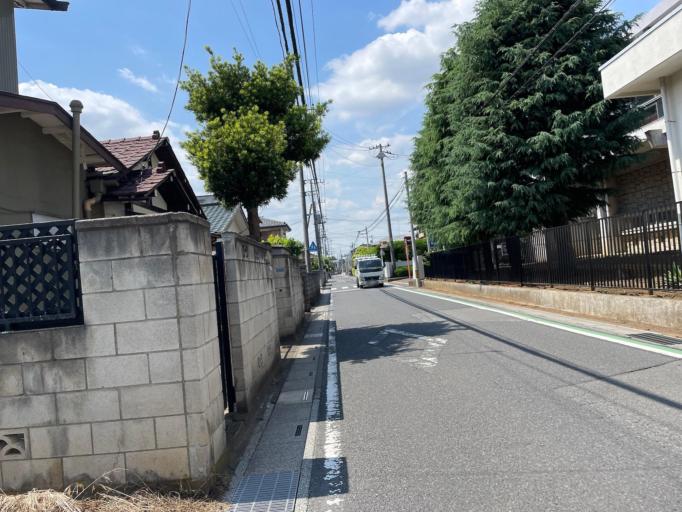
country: JP
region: Saitama
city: Iwatsuki
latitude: 35.9501
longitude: 139.7045
